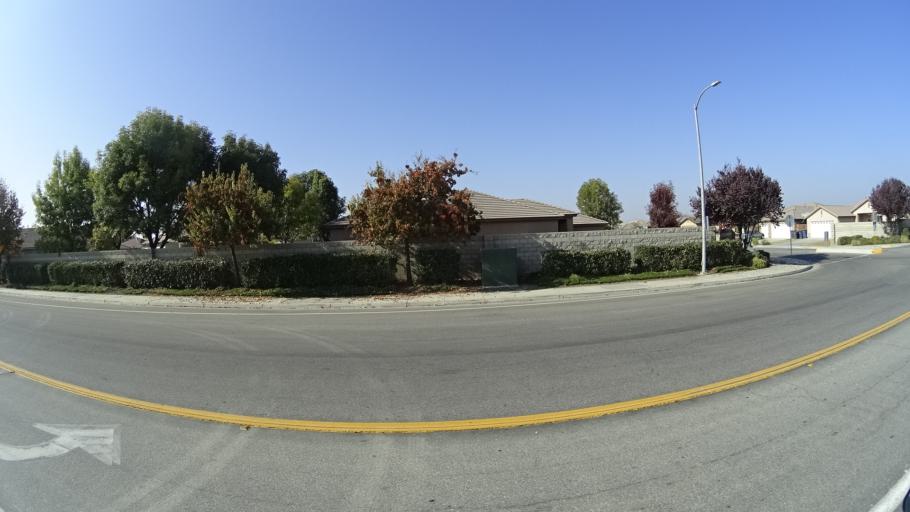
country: US
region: California
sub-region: Kern County
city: Greenfield
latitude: 35.2695
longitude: -119.0390
